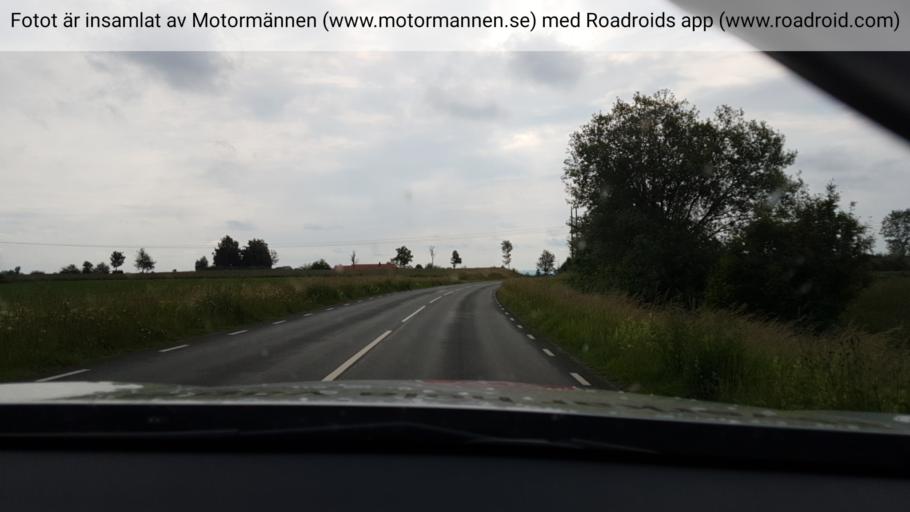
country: SE
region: Vaestra Goetaland
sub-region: Skovde Kommun
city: Skultorp
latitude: 58.3299
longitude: 13.7910
